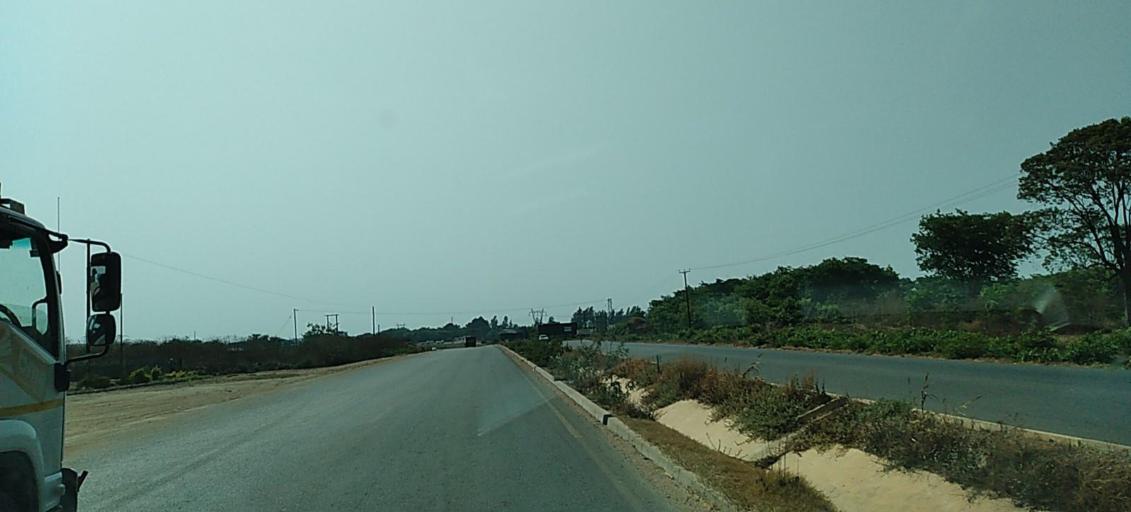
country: ZM
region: Copperbelt
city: Chingola
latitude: -12.5617
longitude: 27.8806
